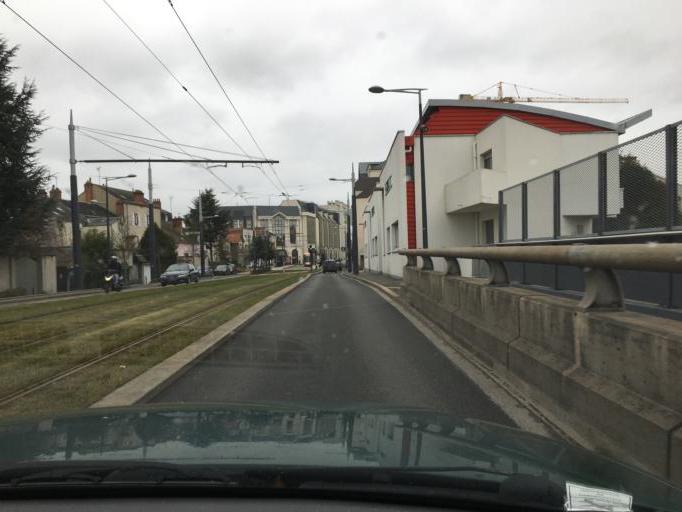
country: FR
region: Centre
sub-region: Departement du Loiret
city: Orleans
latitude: 47.9126
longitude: 1.9151
